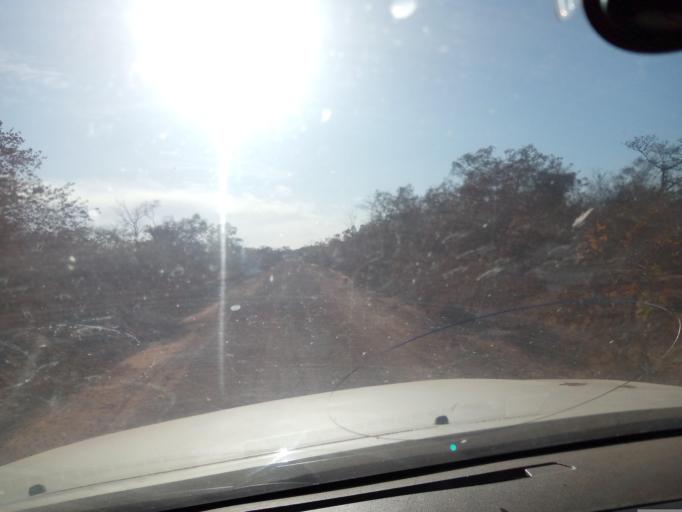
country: ML
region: Sikasso
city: Sikasso
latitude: 11.4785
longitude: -5.4973
